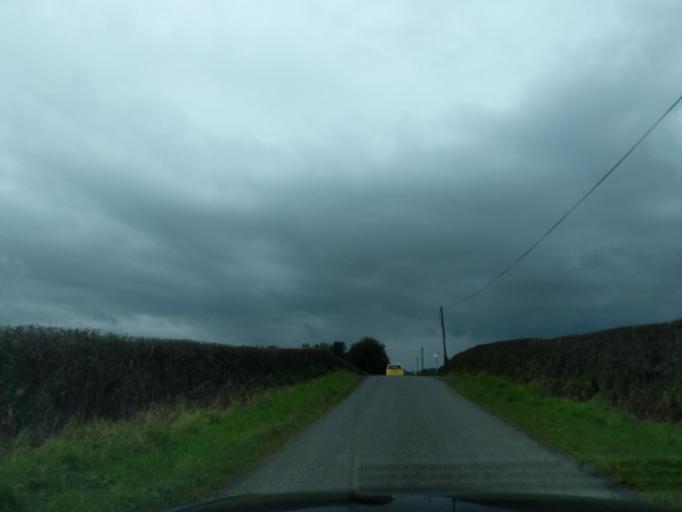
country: GB
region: Scotland
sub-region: Dumfries and Galloway
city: Castle Douglas
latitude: 54.9091
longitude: -3.9774
